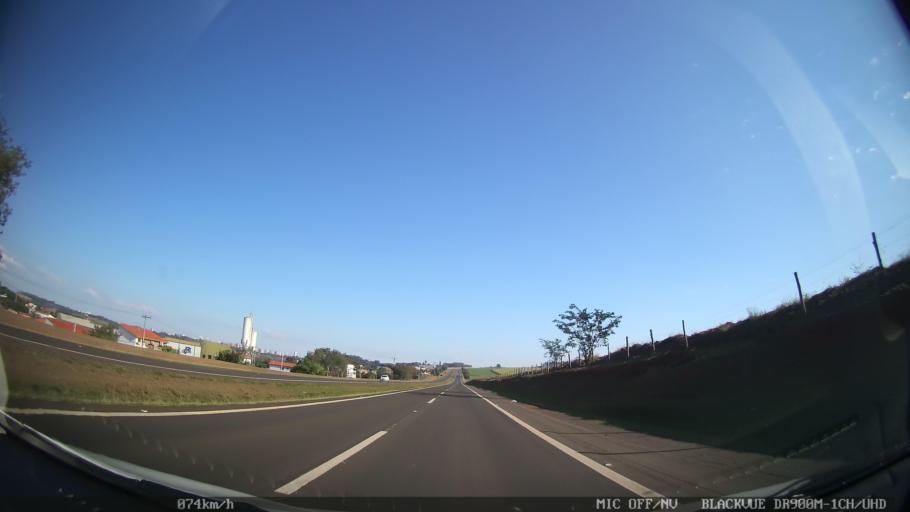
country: BR
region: Sao Paulo
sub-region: Piracicaba
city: Piracicaba
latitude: -22.6785
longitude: -47.6347
